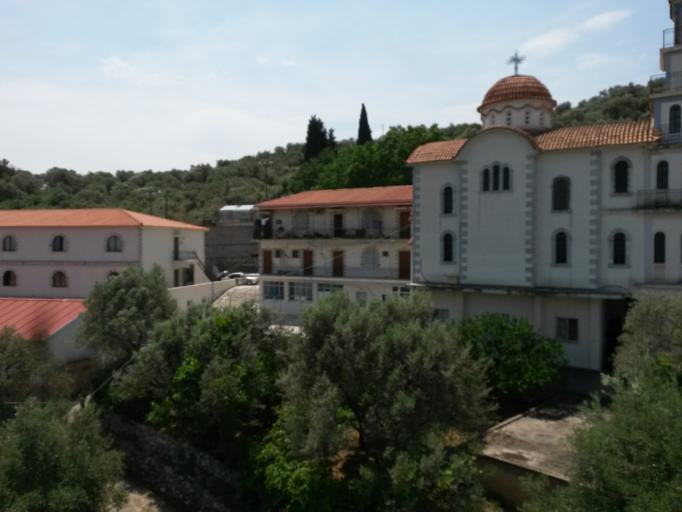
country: GR
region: North Aegean
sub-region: Nomos Lesvou
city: Pamfylla
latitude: 39.1707
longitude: 26.4819
